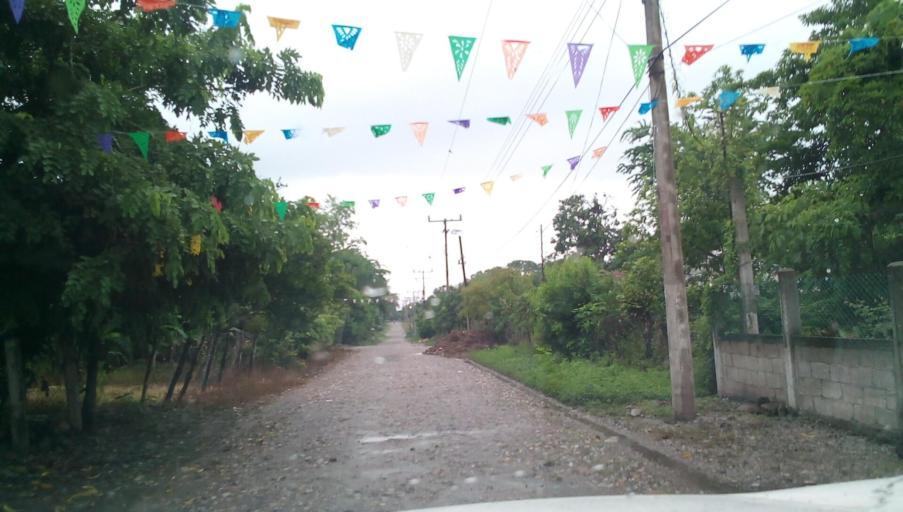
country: MX
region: Veracruz
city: Tempoal de Sanchez
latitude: 21.4173
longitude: -98.4272
